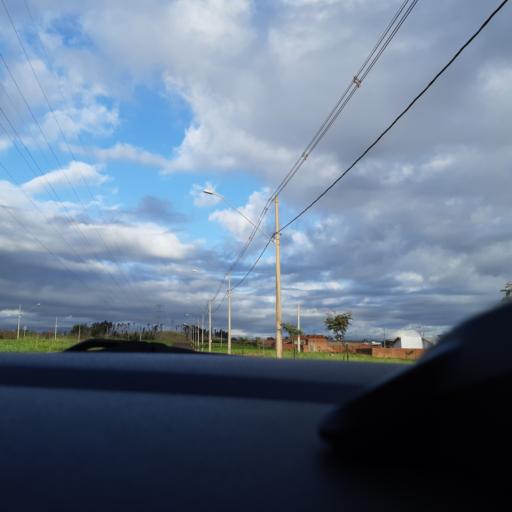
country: BR
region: Sao Paulo
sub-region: Ourinhos
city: Ourinhos
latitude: -23.0015
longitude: -49.8423
